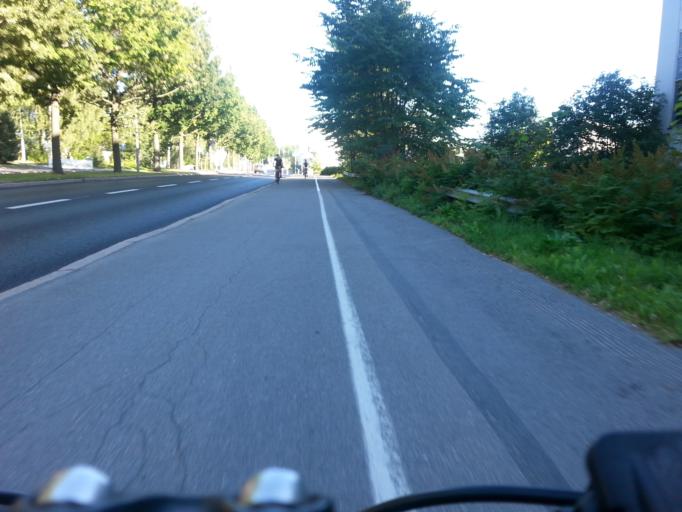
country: FI
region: Uusimaa
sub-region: Helsinki
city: Teekkarikylae
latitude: 60.2164
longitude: 24.8715
